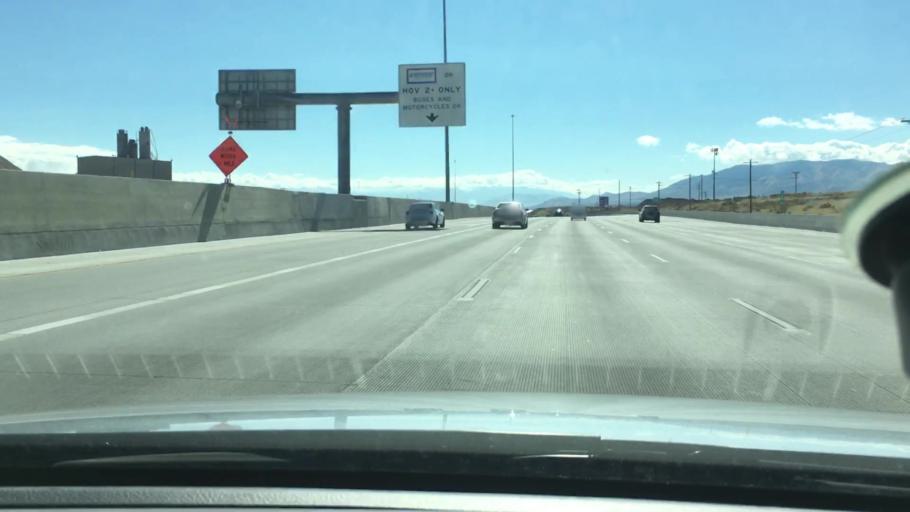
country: US
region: Utah
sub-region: Salt Lake County
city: Bluffdale
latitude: 40.4541
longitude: -111.9139
